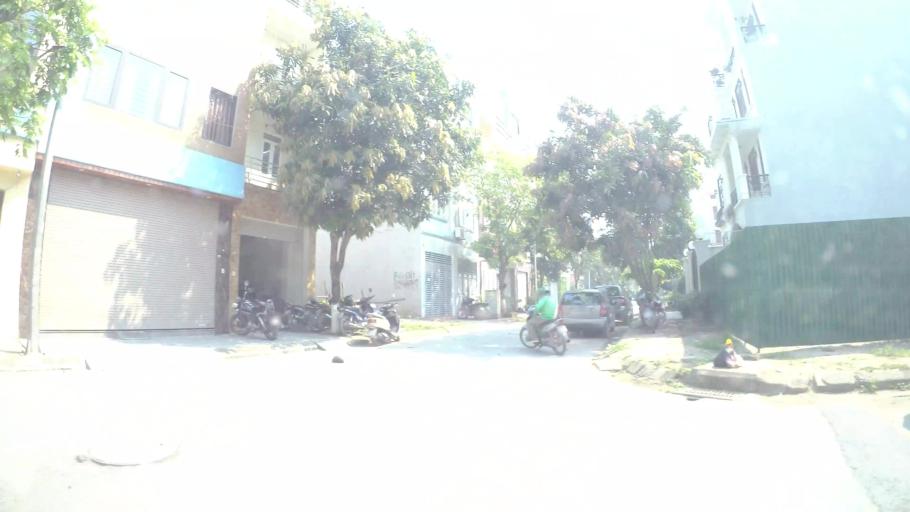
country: VN
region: Ha Noi
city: Ha Dong
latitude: 20.9548
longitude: 105.8078
